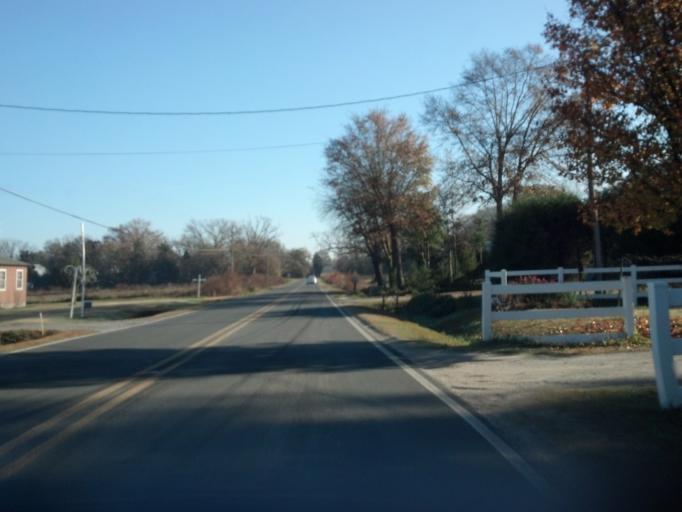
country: US
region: North Carolina
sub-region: Pitt County
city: Winterville
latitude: 35.5168
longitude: -77.4514
